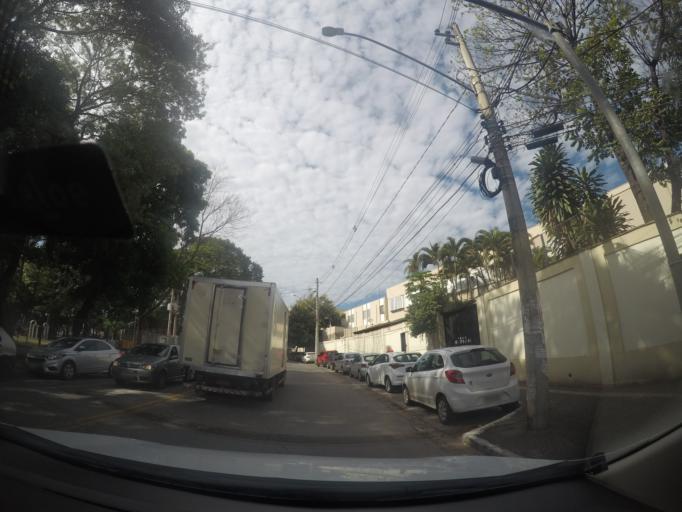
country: BR
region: Goias
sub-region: Goiania
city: Goiania
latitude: -16.6672
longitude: -49.2548
